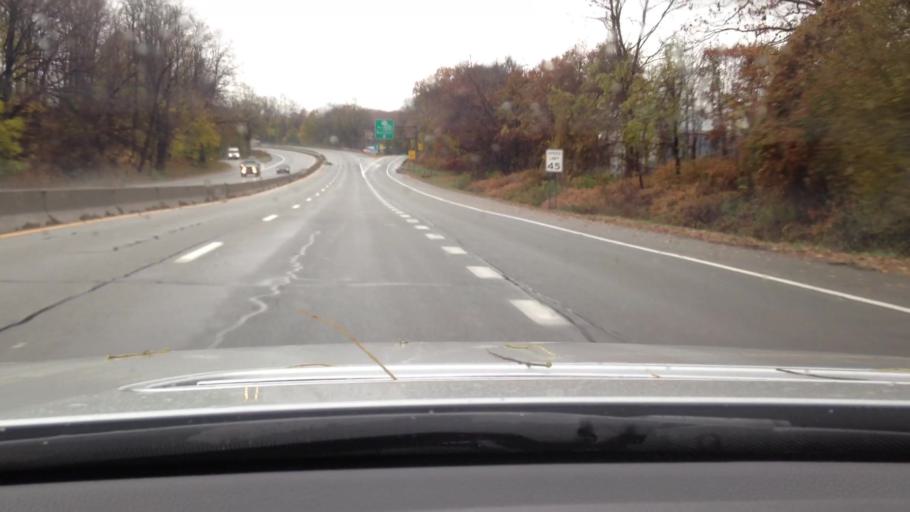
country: US
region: New York
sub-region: Westchester County
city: Buchanan
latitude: 41.2740
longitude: -73.9325
